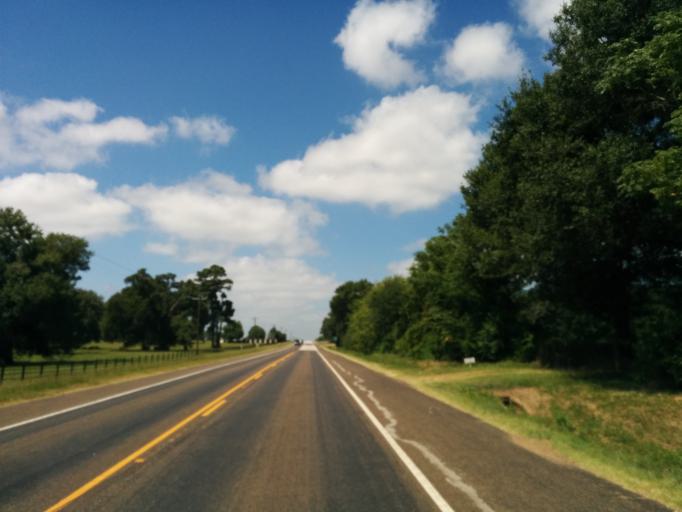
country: US
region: Texas
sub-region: Houston County
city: Crockett
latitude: 31.2979
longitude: -95.4945
